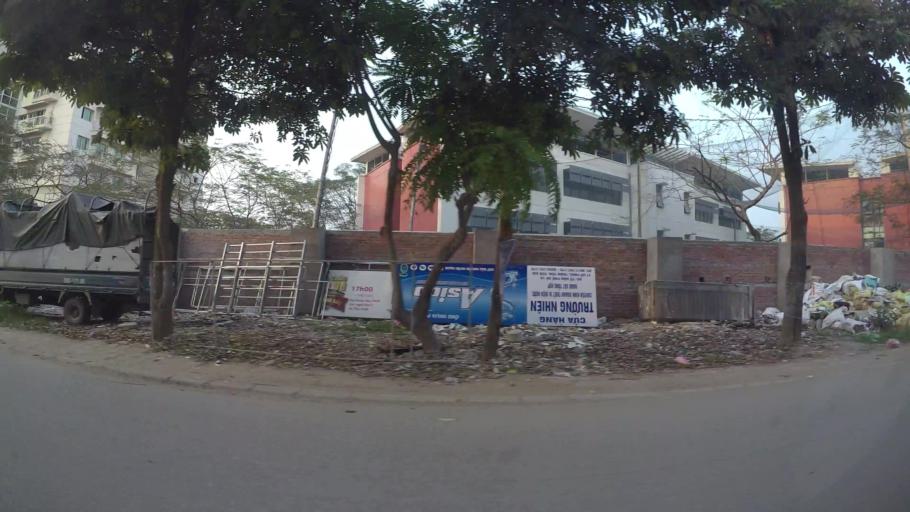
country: VN
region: Ha Noi
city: Tay Ho
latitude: 21.0732
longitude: 105.8018
